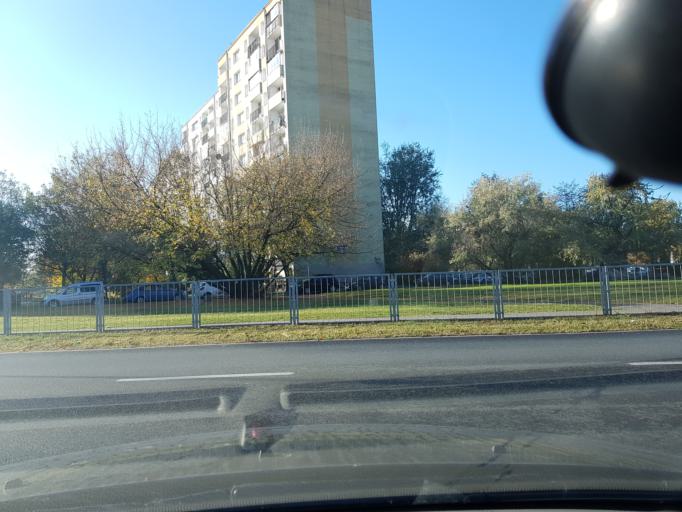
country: PL
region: Masovian Voivodeship
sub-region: Warszawa
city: Bielany
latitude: 52.2883
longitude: 20.9353
